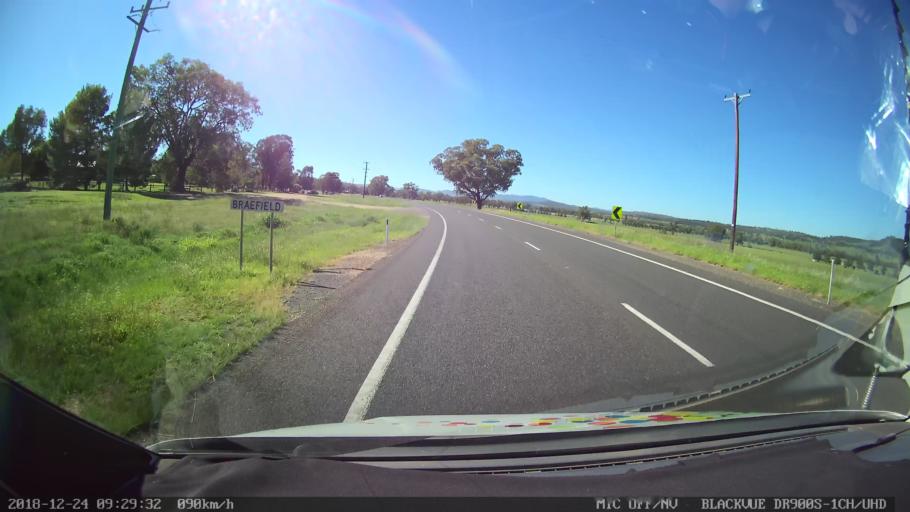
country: AU
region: New South Wales
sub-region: Liverpool Plains
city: Quirindi
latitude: -31.5517
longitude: 150.6920
